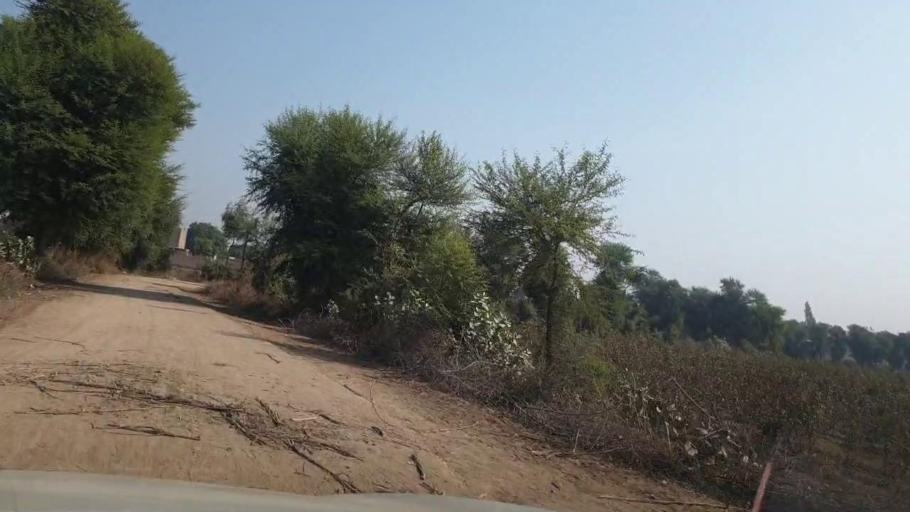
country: PK
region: Sindh
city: Bhan
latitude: 26.5437
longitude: 67.7747
